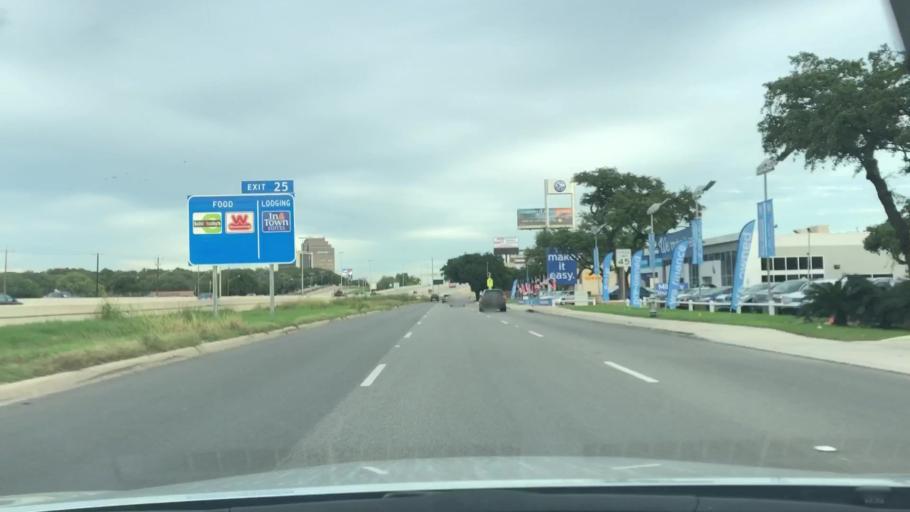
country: US
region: Texas
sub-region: Bexar County
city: Alamo Heights
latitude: 29.5158
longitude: -98.4467
